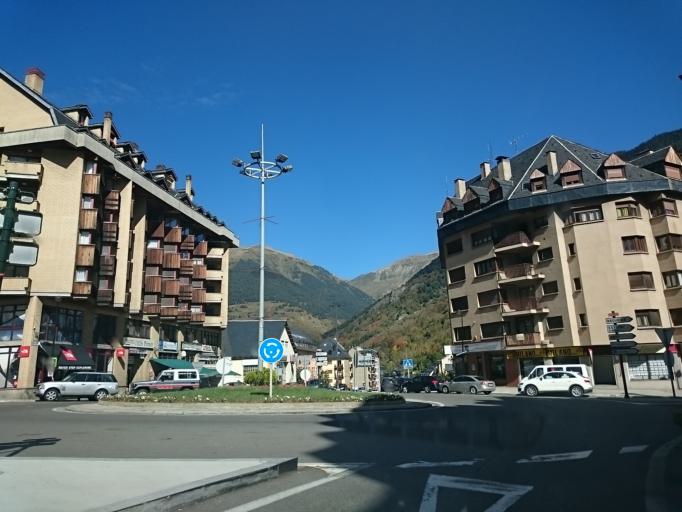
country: ES
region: Catalonia
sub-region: Provincia de Lleida
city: Vielha
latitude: 42.7028
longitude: 0.7932
